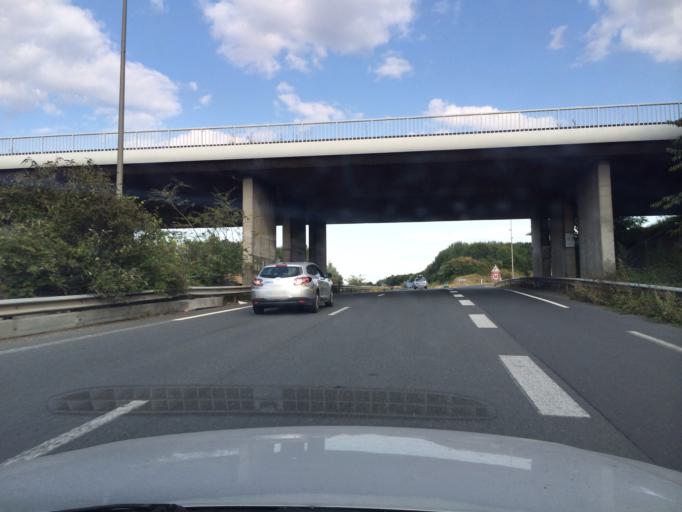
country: FR
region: Lower Normandy
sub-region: Departement du Calvados
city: Giberville
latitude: 49.1693
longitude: -0.3015
